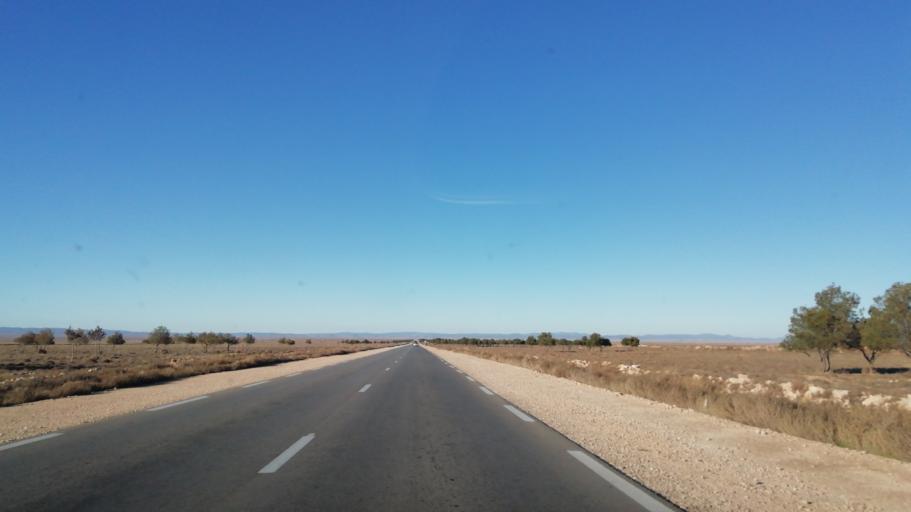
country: DZ
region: Tlemcen
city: Sebdou
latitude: 34.3290
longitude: -1.2641
